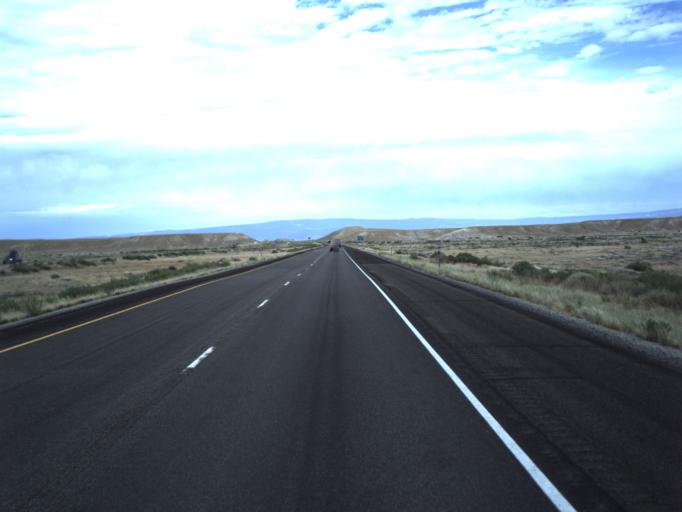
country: US
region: Utah
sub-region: Grand County
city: Moab
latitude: 38.9445
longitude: -109.6470
